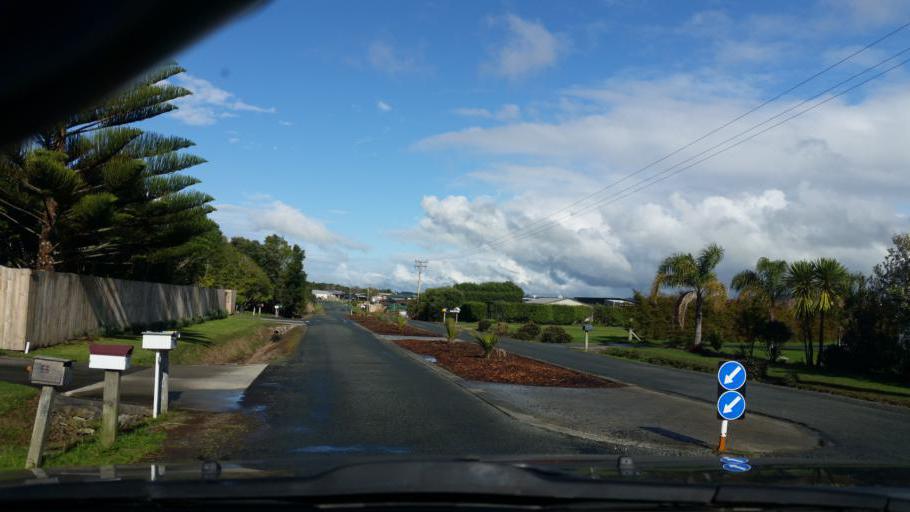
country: NZ
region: Auckland
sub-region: Auckland
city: Wellsford
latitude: -36.0908
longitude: 174.5731
